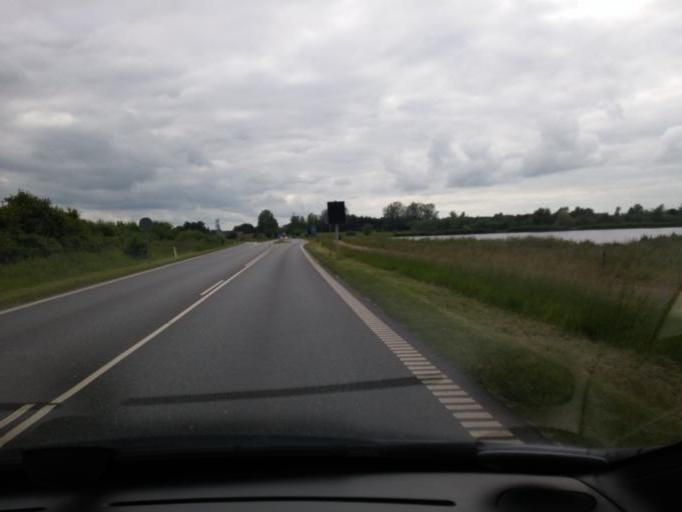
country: DK
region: Capital Region
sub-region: Hillerod Kommune
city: Hillerod
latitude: 55.9551
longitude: 12.2654
